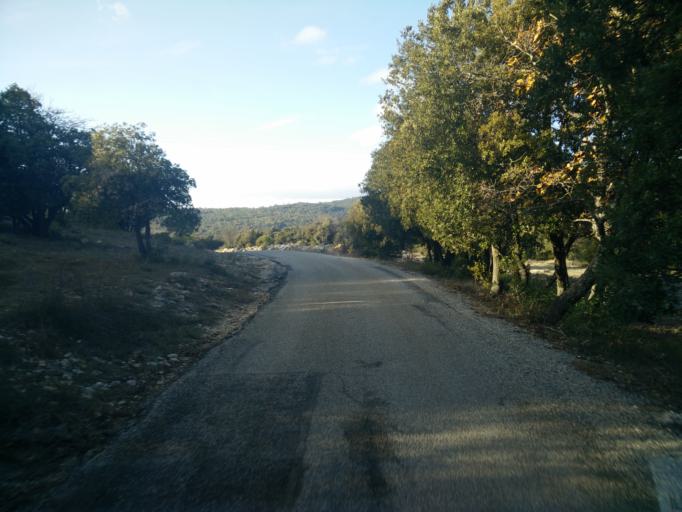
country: FR
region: Provence-Alpes-Cote d'Azur
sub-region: Departement du Var
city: Le Revest-les-Eaux
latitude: 43.2261
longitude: 5.9307
